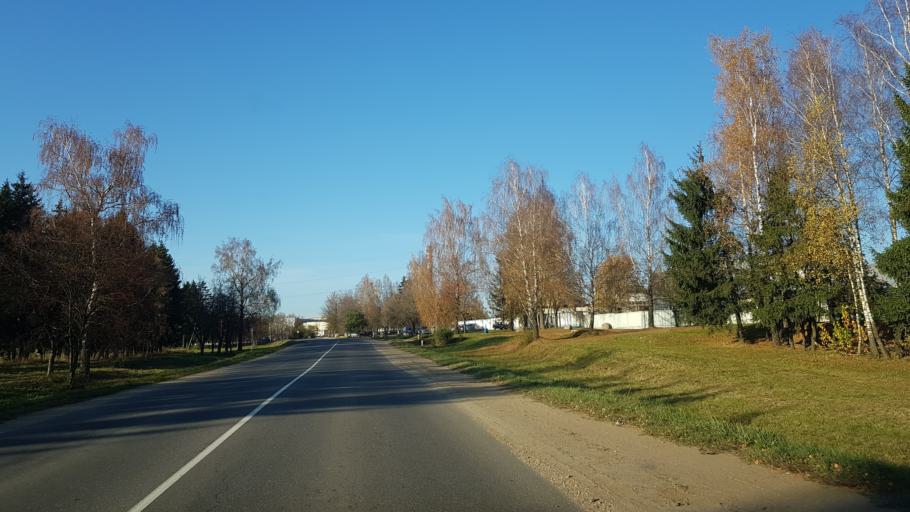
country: BY
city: Fanipol
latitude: 53.7319
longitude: 27.3320
